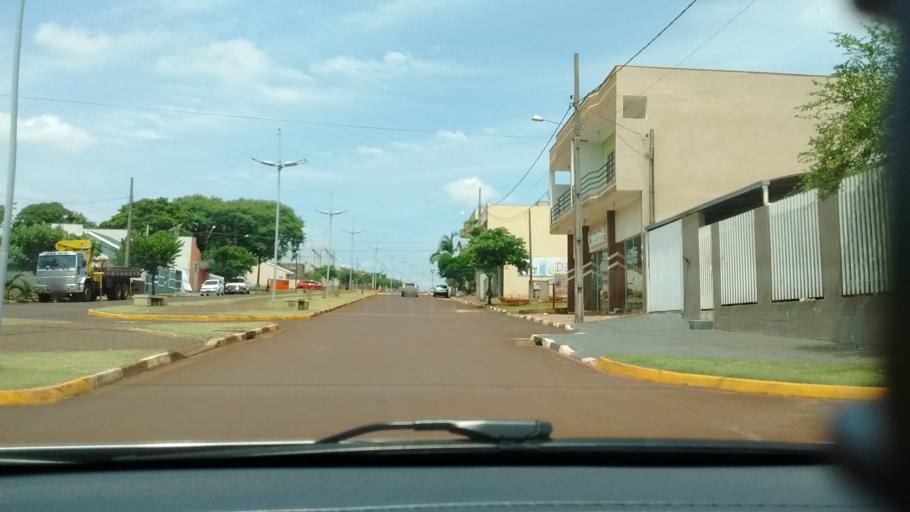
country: BR
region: Parana
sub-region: Corbelia
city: Corbelia
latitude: -24.5503
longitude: -52.9903
